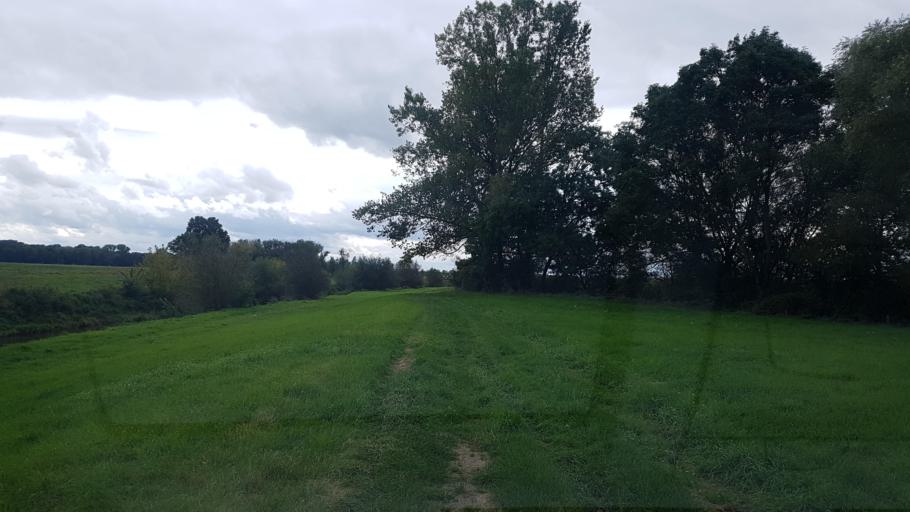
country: DE
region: Saxony
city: Pegau
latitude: 51.1526
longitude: 12.2614
